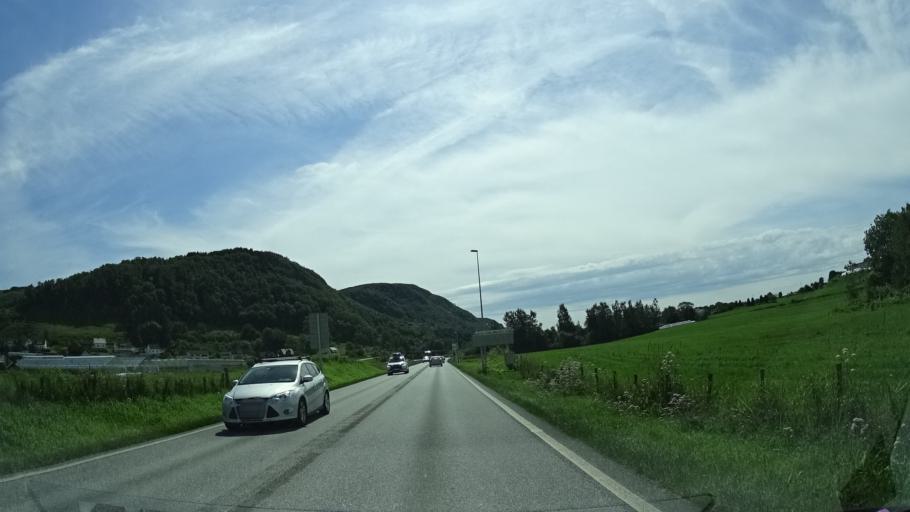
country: NO
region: Rogaland
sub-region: Rennesoy
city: Vikevag
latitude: 59.1095
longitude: 5.6997
